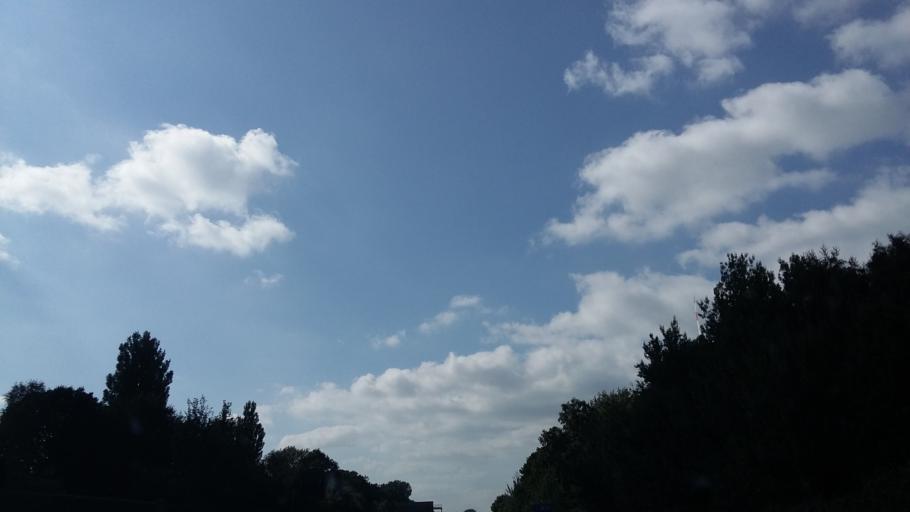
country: DE
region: Bremen
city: Bremen
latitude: 53.1189
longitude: 8.7993
